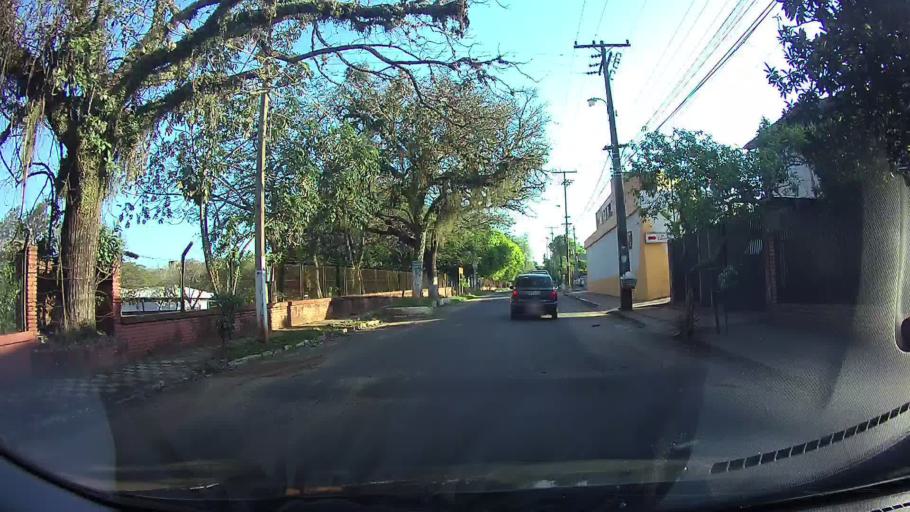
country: PY
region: Central
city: Fernando de la Mora
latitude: -25.3398
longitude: -57.5308
